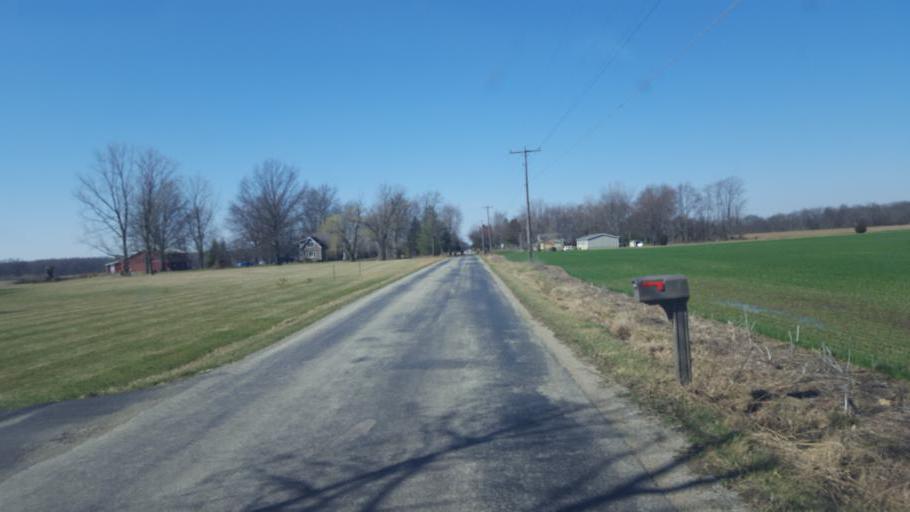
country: US
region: Ohio
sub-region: Morrow County
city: Cardington
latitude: 40.4968
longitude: -82.8446
